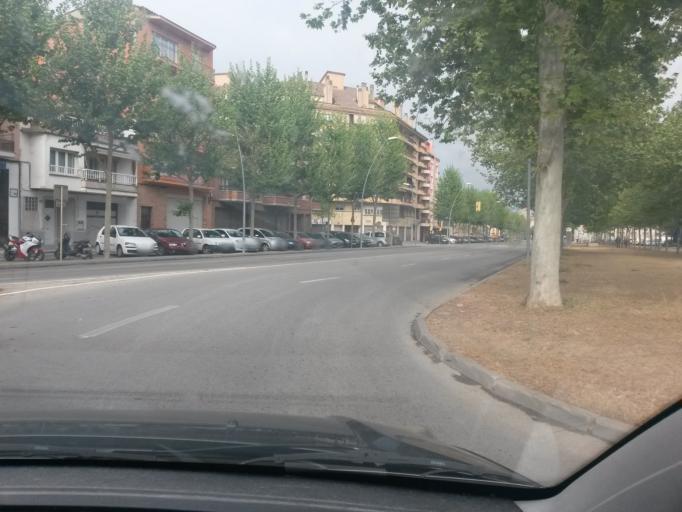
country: ES
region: Catalonia
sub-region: Provincia de Girona
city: Salt
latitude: 41.9709
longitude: 2.7821
